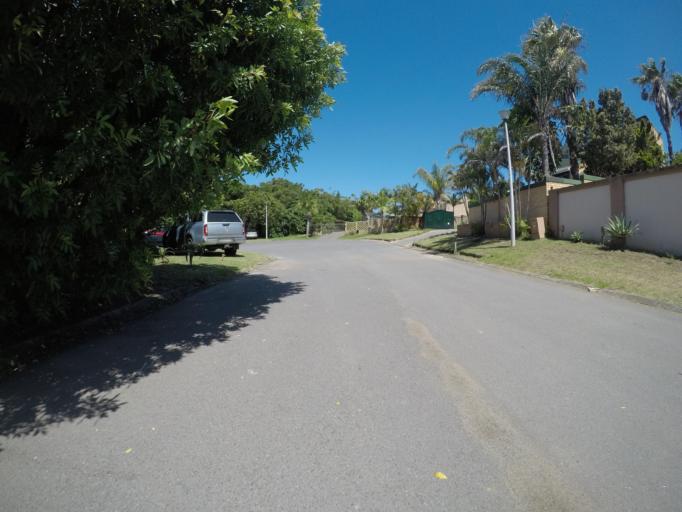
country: ZA
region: Eastern Cape
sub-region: Buffalo City Metropolitan Municipality
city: East London
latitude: -32.9711
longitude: 27.9439
